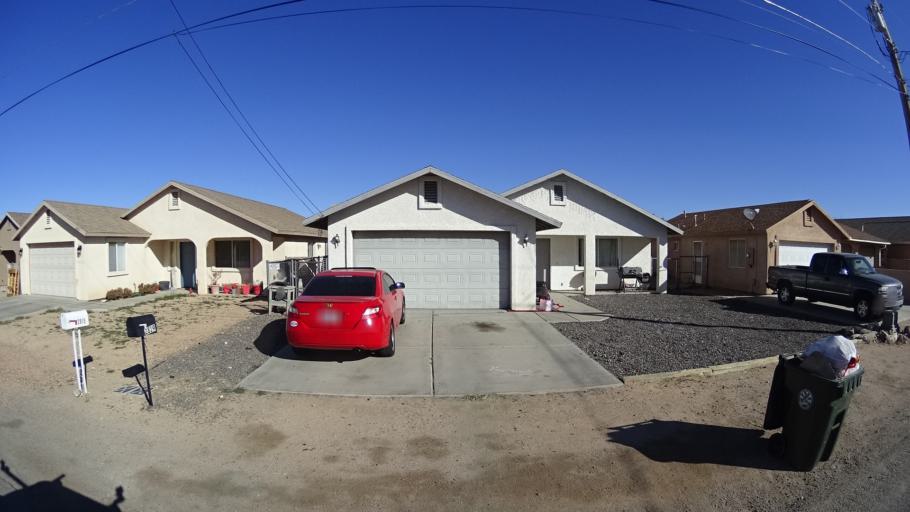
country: US
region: Arizona
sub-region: Mohave County
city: Kingman
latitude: 35.2055
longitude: -114.0129
